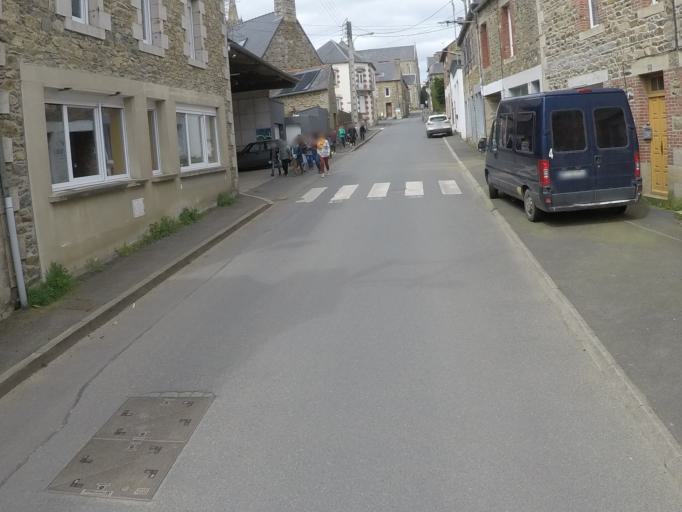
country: FR
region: Brittany
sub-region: Departement des Cotes-d'Armor
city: Plouha
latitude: 48.6746
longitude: -2.9272
